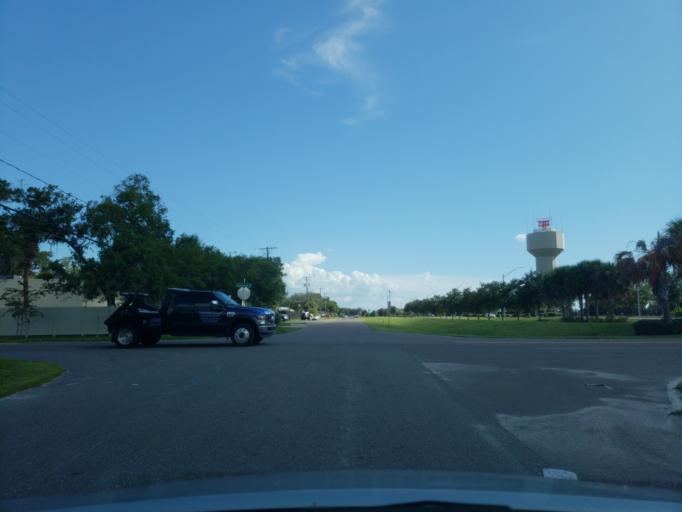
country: US
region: Florida
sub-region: Hillsborough County
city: Egypt Lake-Leto
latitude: 27.9893
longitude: -82.5195
